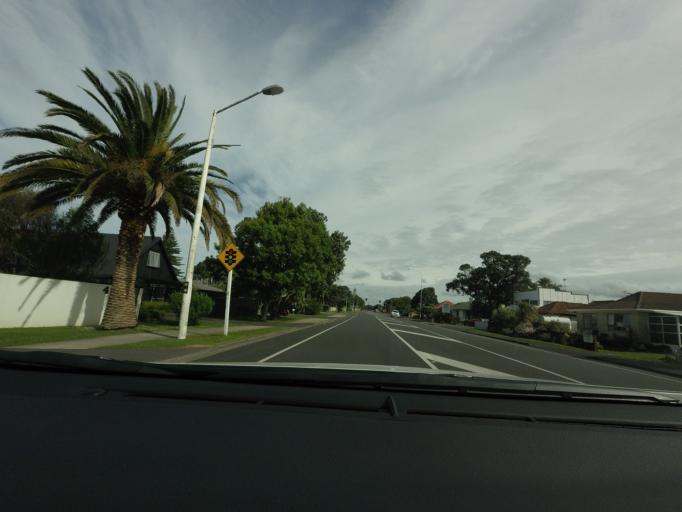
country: NZ
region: Auckland
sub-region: Auckland
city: Rothesay Bay
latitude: -36.5793
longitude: 174.6924
